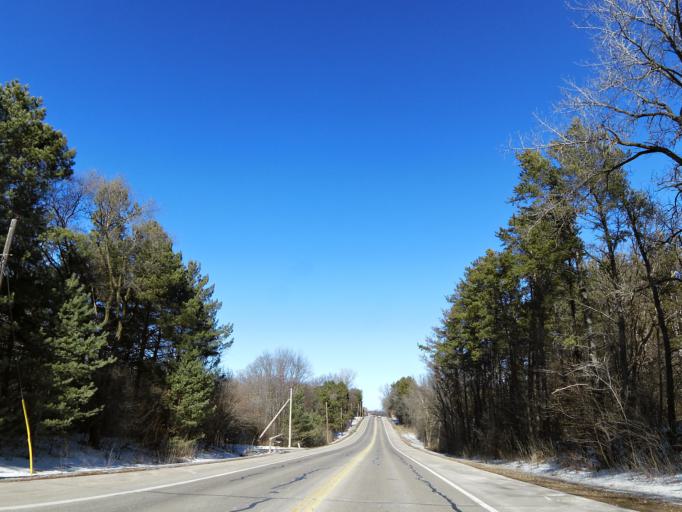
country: US
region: Minnesota
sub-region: Washington County
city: Grant
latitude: 45.0459
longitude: -92.8835
